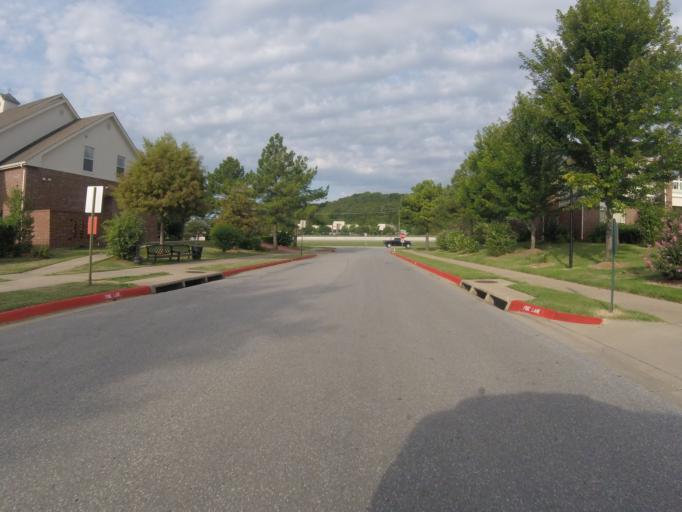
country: US
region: Arkansas
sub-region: Washington County
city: Fayetteville
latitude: 36.0597
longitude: -94.1961
